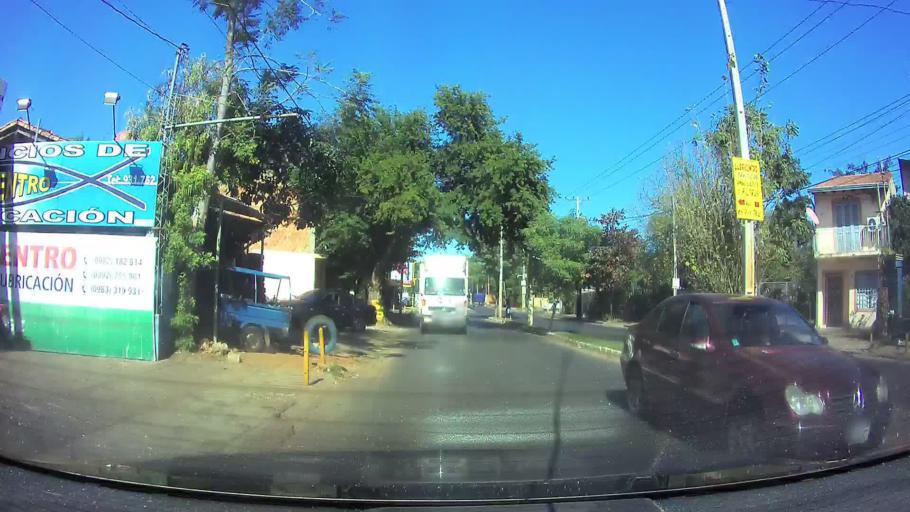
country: PY
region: Central
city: Villa Elisa
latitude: -25.3668
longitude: -57.5784
